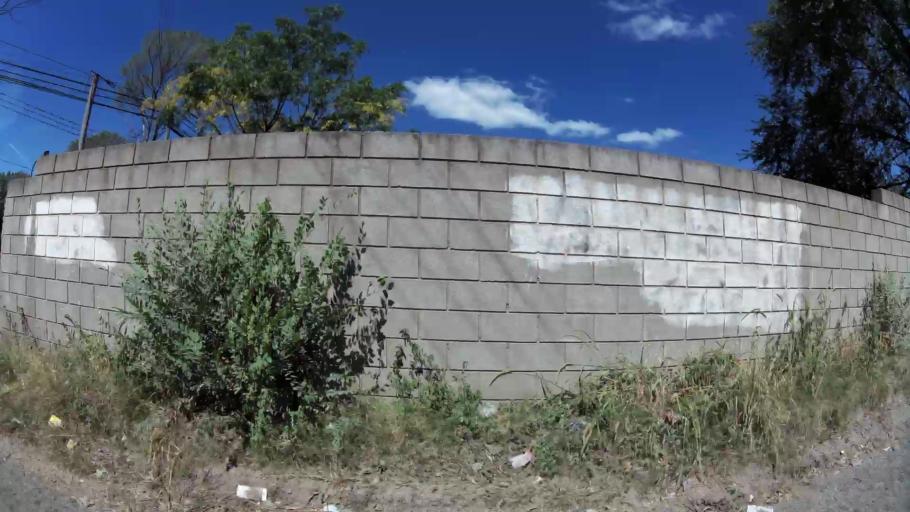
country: AR
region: Cordoba
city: Villa Allende
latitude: -31.2915
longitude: -64.3039
